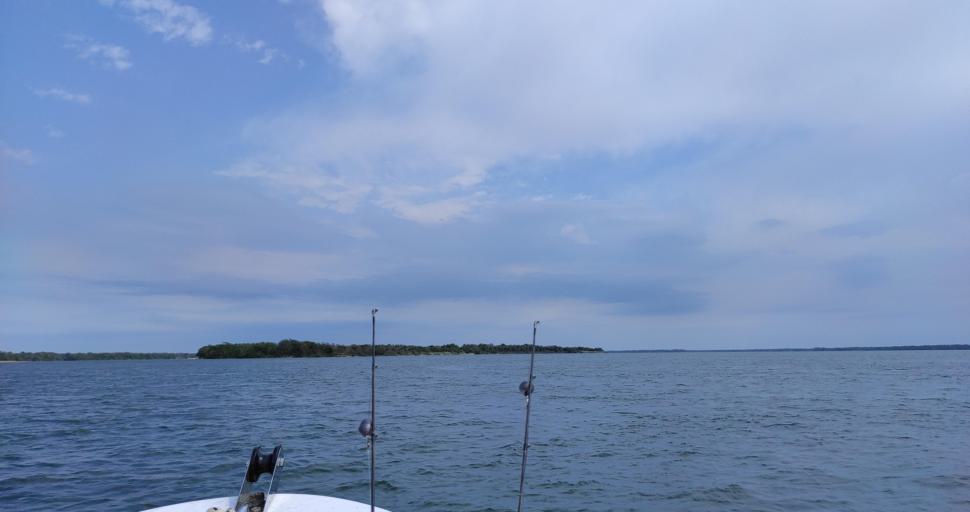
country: PY
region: Neembucu
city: Cerrito
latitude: -27.3621
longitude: -57.6675
